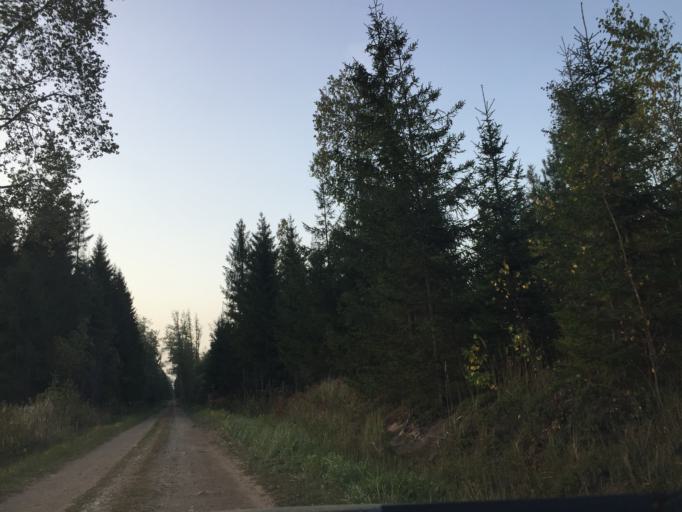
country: LV
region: Ikskile
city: Ikskile
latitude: 56.9316
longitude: 24.4873
